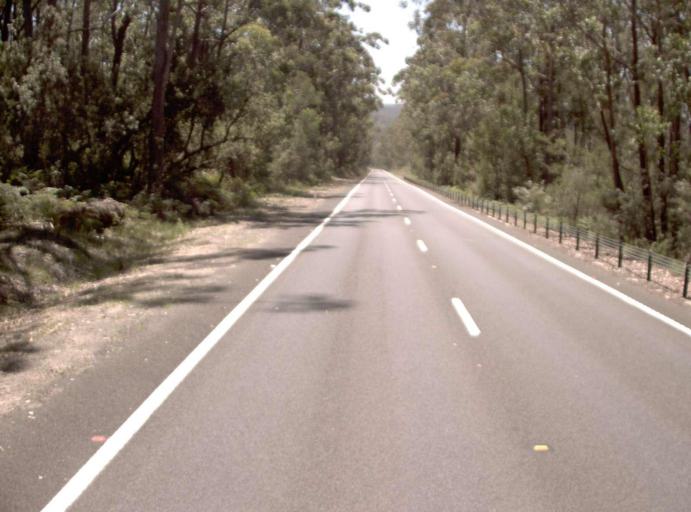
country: AU
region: Victoria
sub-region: East Gippsland
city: Lakes Entrance
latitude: -37.7433
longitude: 148.0756
